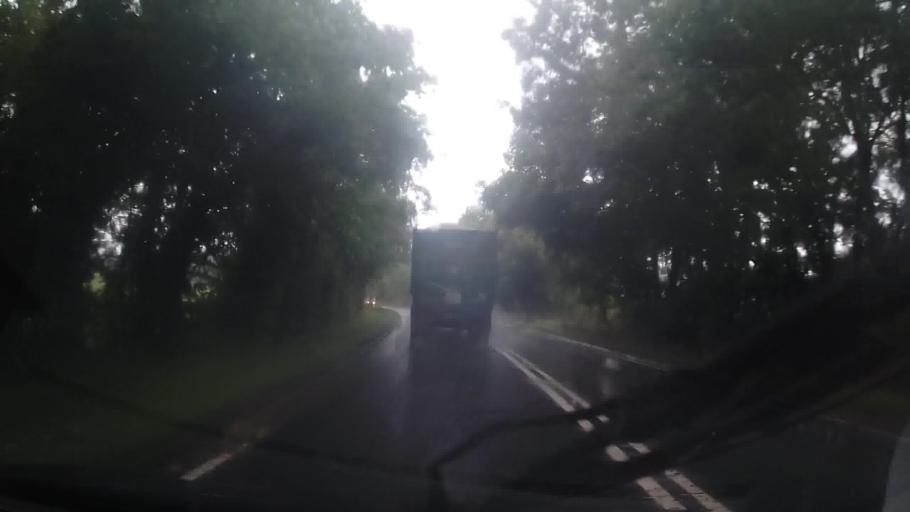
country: GB
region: England
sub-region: Worcestershire
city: Evesham
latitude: 52.1255
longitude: -1.9933
